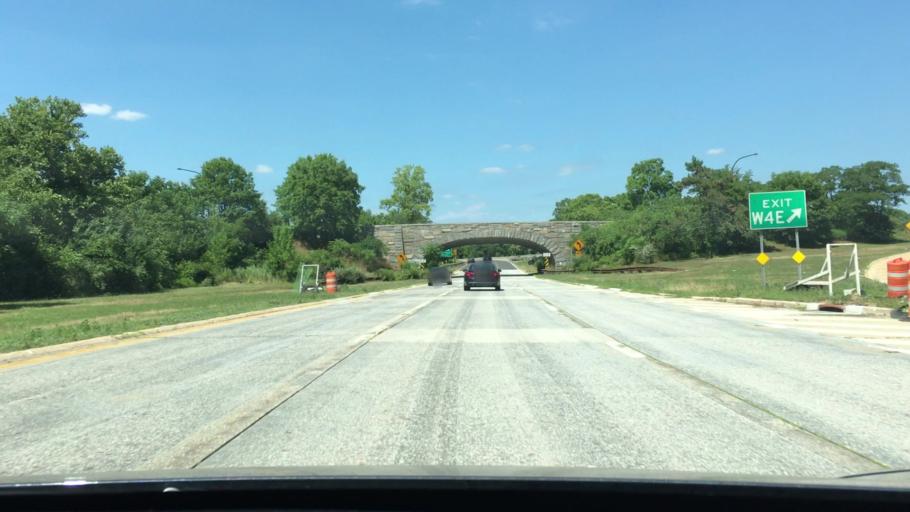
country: US
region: New York
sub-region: Nassau County
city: North Wantagh
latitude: 40.6961
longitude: -73.5196
